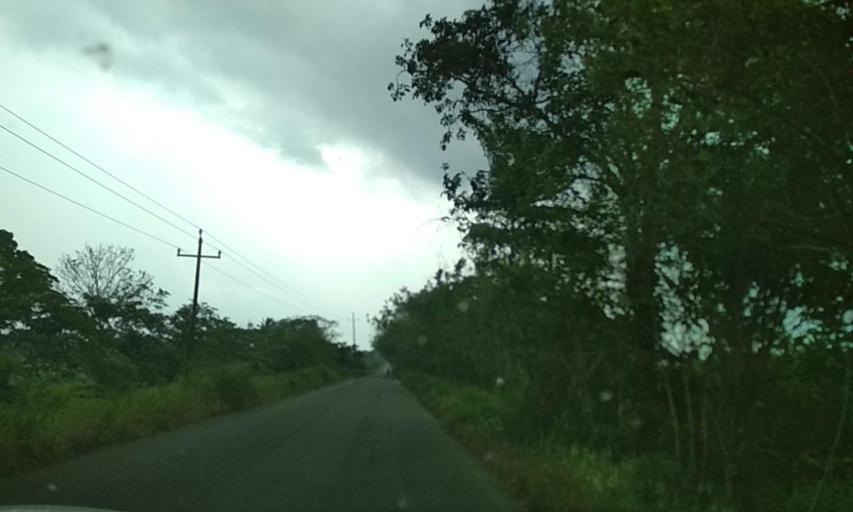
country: MX
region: Tabasco
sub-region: Huimanguillo
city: Francisco Rueda
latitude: 17.5590
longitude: -94.1188
